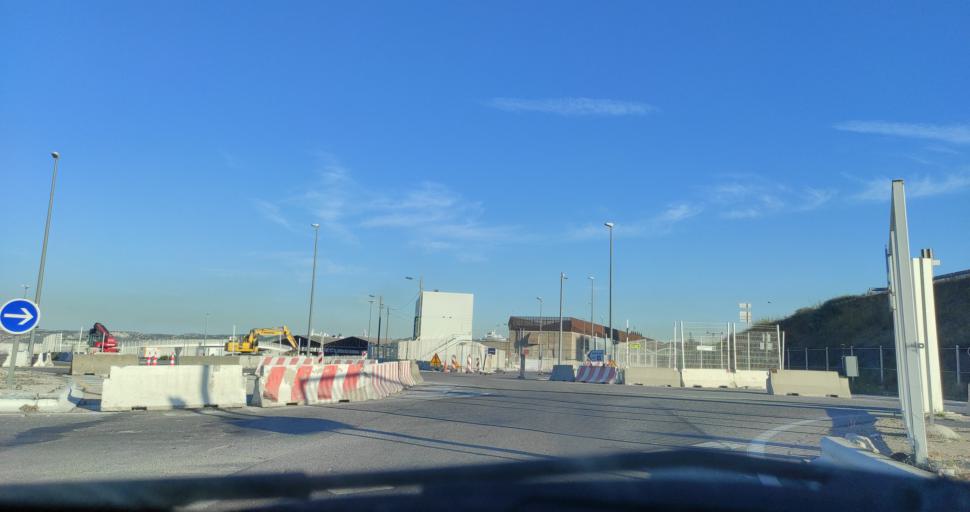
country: FR
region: Provence-Alpes-Cote d'Azur
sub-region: Departement des Bouches-du-Rhone
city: Marseille 16
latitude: 43.3358
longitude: 5.3505
